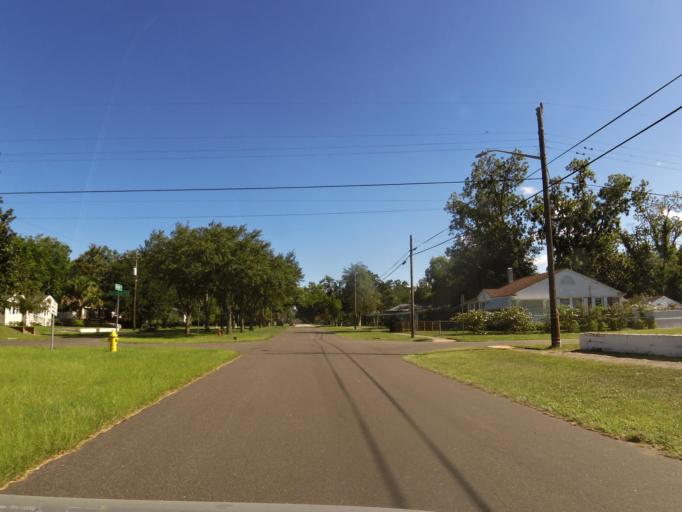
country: US
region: Florida
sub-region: Duval County
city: Jacksonville
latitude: 30.2766
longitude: -81.7262
